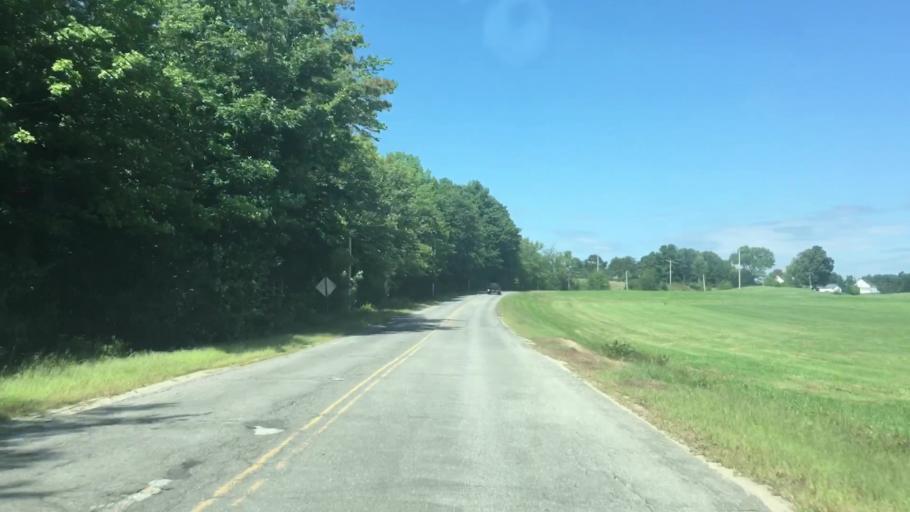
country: US
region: Maine
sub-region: Androscoggin County
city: Lisbon
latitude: 44.0712
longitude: -70.1146
